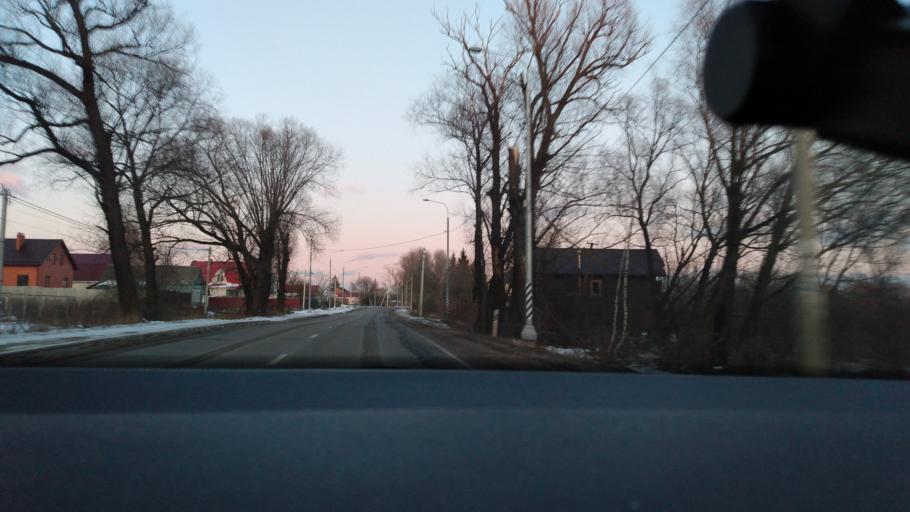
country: RU
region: Moskovskaya
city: Krasnaya Poyma
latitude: 55.1039
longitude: 38.9981
